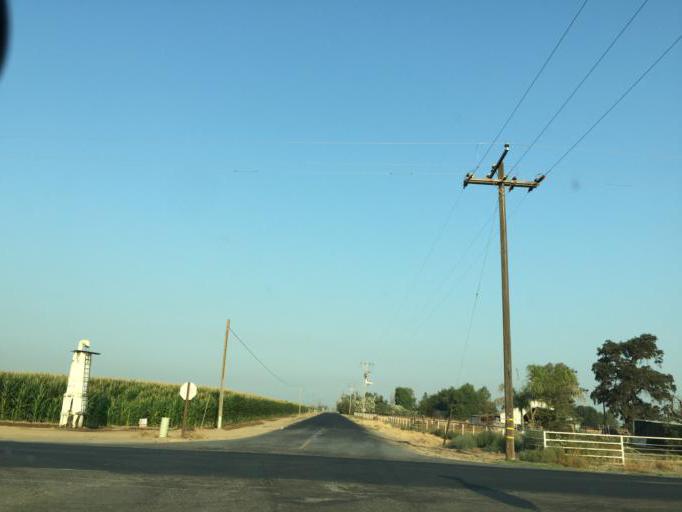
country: US
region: California
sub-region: Tulare County
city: Cutler
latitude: 36.4290
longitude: -119.3226
